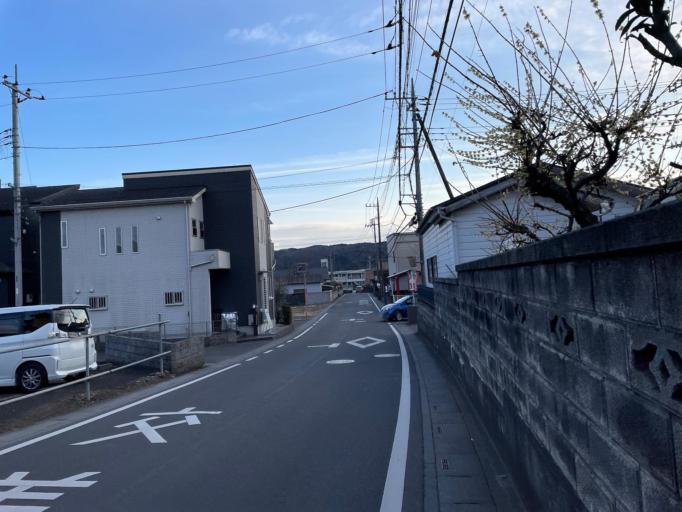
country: JP
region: Saitama
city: Hanno
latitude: 35.8423
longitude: 139.3475
